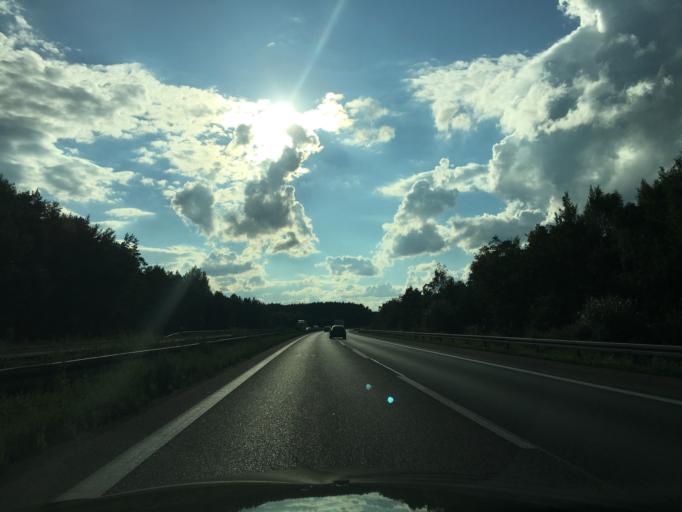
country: DE
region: Bavaria
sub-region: Regierungsbezirk Mittelfranken
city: Kammerstein
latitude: 49.3030
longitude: 10.9305
